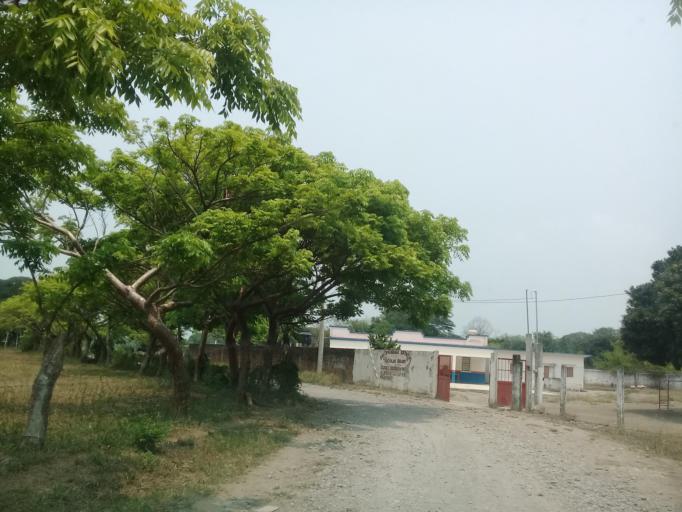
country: MX
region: Veracruz
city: Jamapa
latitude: 18.9316
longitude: -96.2111
